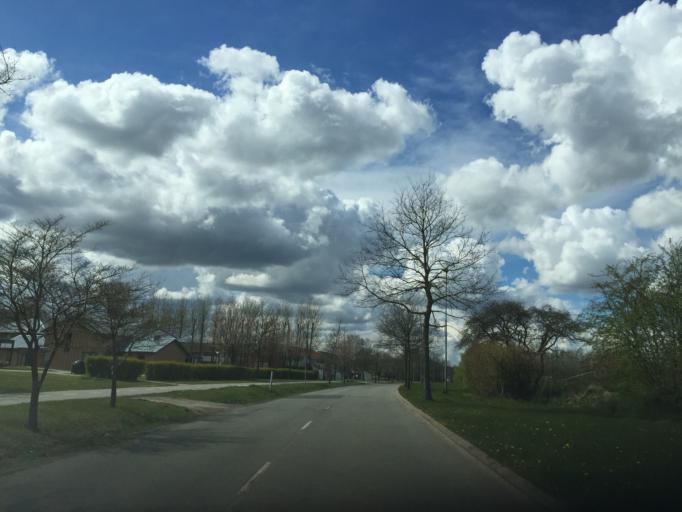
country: DK
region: South Denmark
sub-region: Odense Kommune
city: Odense
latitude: 55.3681
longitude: 10.4088
